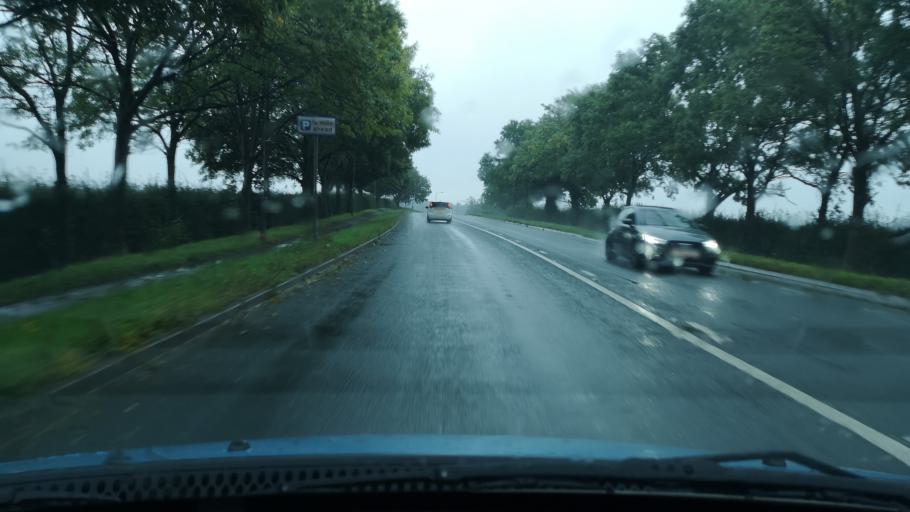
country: GB
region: England
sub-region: City and Borough of Wakefield
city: Fitzwilliam
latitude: 53.6458
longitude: -1.3668
